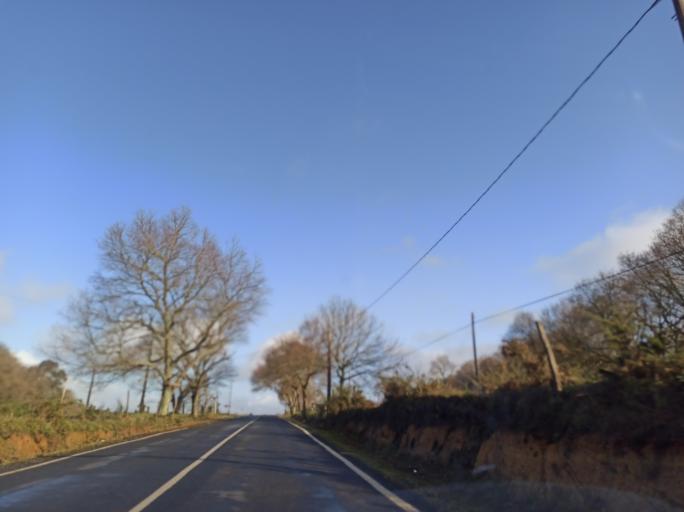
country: ES
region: Galicia
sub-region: Provincia da Coruna
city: Curtis
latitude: 43.0942
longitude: -7.9923
